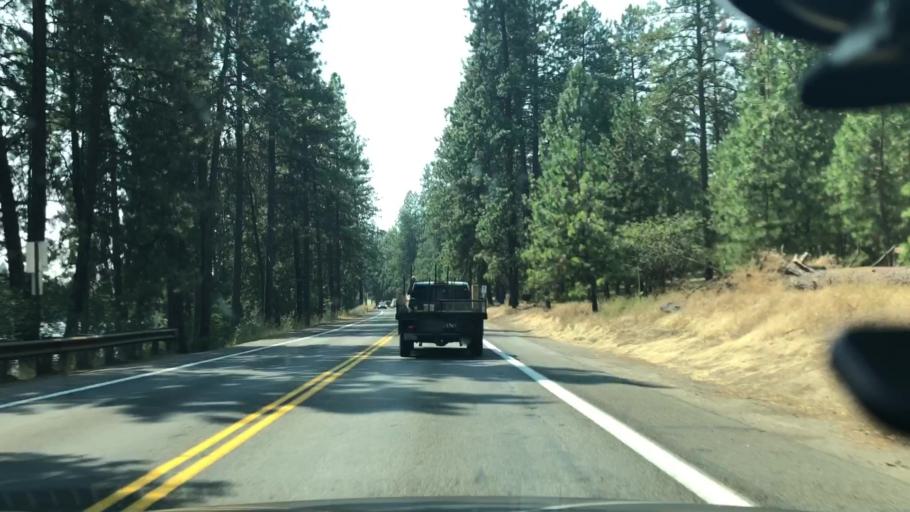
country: US
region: Washington
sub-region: Spokane County
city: Millwood
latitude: 47.6946
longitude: -117.3099
